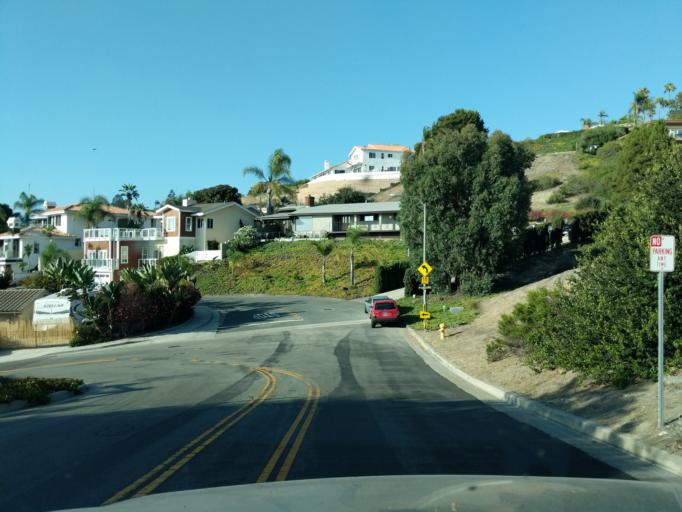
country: US
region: California
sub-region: Orange County
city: San Clemente
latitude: 33.4308
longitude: -117.6127
